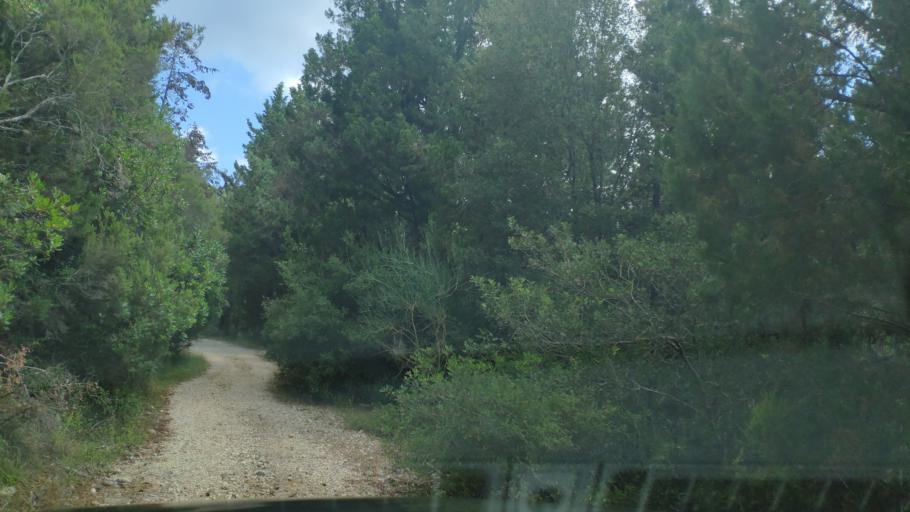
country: GR
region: Ionian Islands
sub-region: Lefkada
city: Lefkada
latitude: 38.8010
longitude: 20.6724
